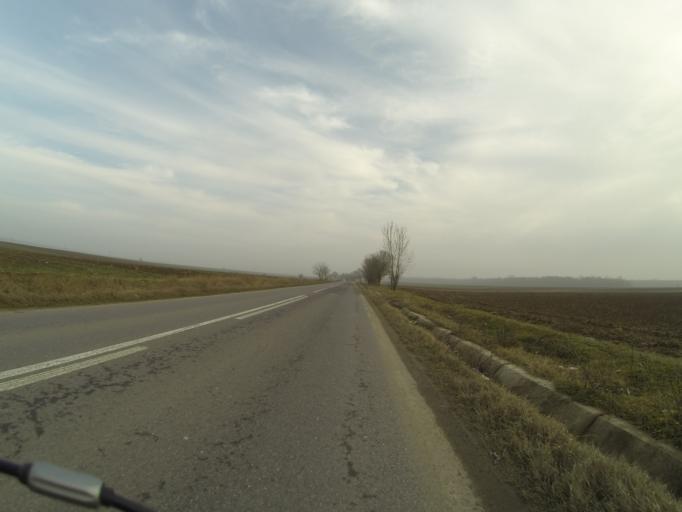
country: RO
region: Mehedinti
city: Vanju-Mare
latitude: 44.4092
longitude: 22.8866
